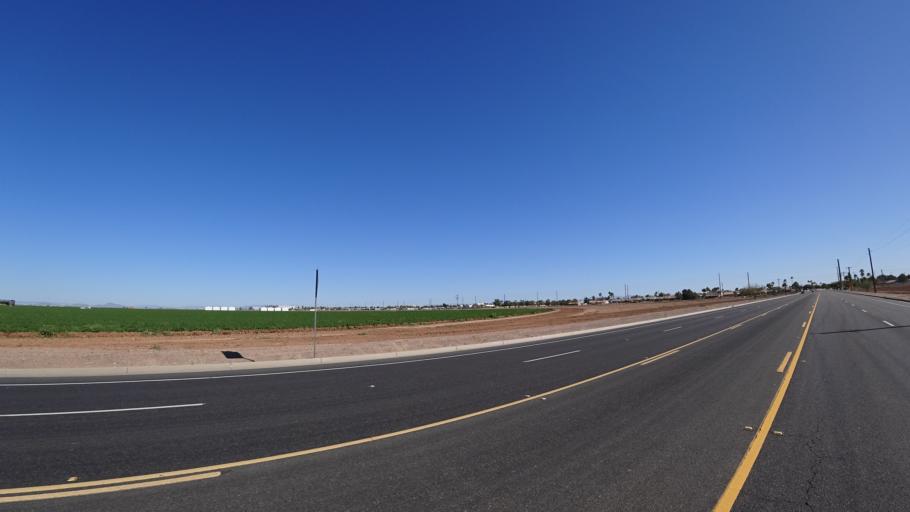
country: US
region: Arizona
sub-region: Maricopa County
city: Sun Lakes
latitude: 33.2192
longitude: -111.8967
